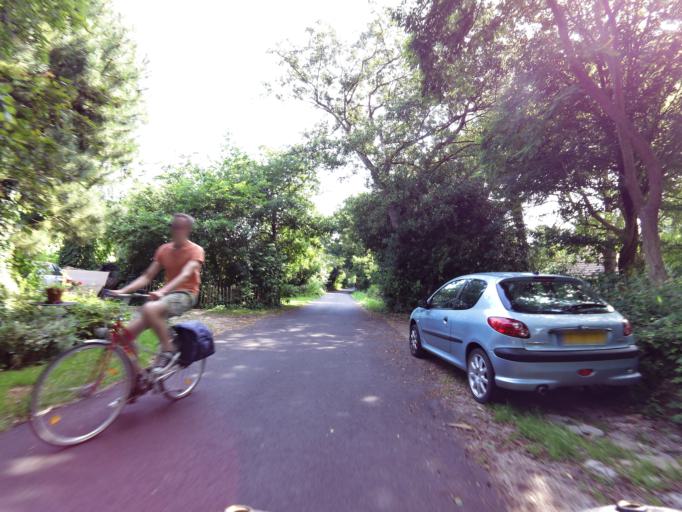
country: NL
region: Zeeland
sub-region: Schouwen-Duiveland
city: Haamstede
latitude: 51.7041
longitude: 3.7317
